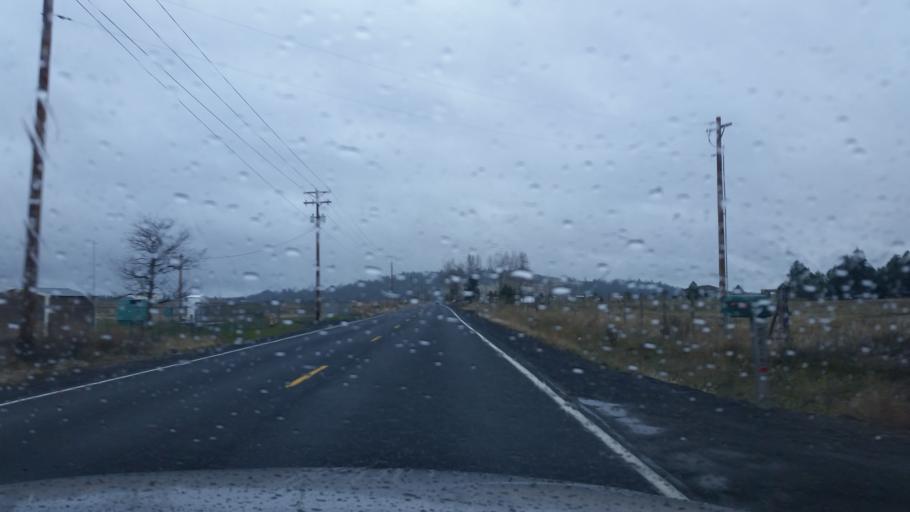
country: US
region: Washington
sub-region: Spokane County
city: Fairchild Air Force Base
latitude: 47.5773
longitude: -117.6076
